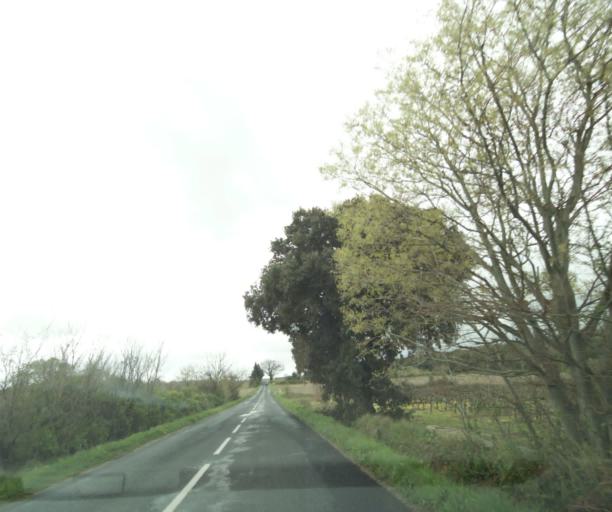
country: FR
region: Languedoc-Roussillon
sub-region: Departement de l'Herault
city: Montbazin
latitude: 43.5341
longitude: 3.6970
